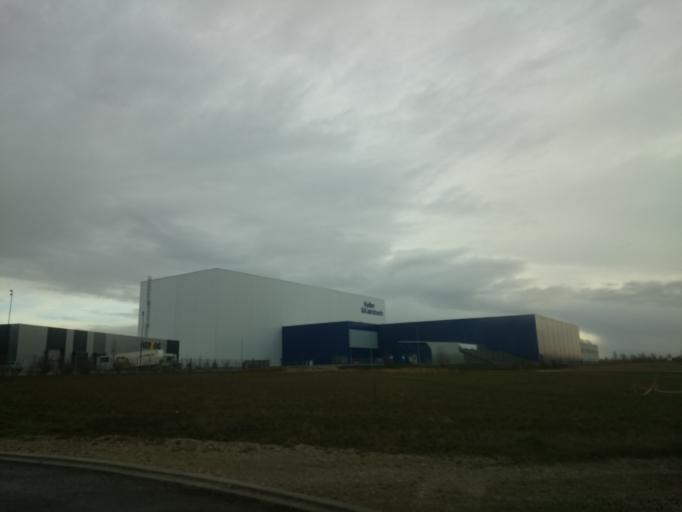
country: DE
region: Bavaria
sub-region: Regierungsbezirk Mittelfranken
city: Hilpoltstein
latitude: 49.1567
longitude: 11.2590
